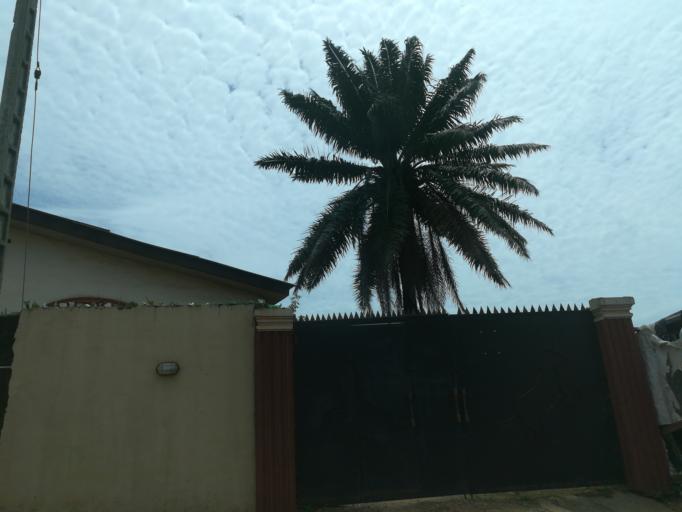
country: NG
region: Lagos
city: Ebute Ikorodu
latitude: 6.5757
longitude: 3.4905
